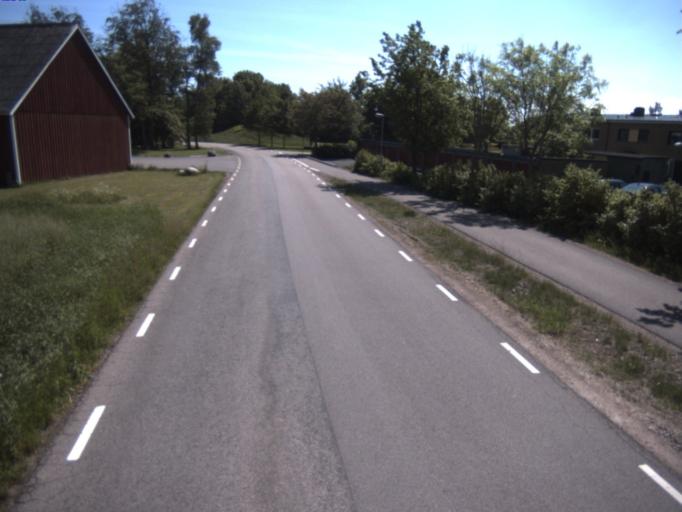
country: SE
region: Skane
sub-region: Helsingborg
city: Barslov
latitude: 56.0107
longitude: 12.8091
